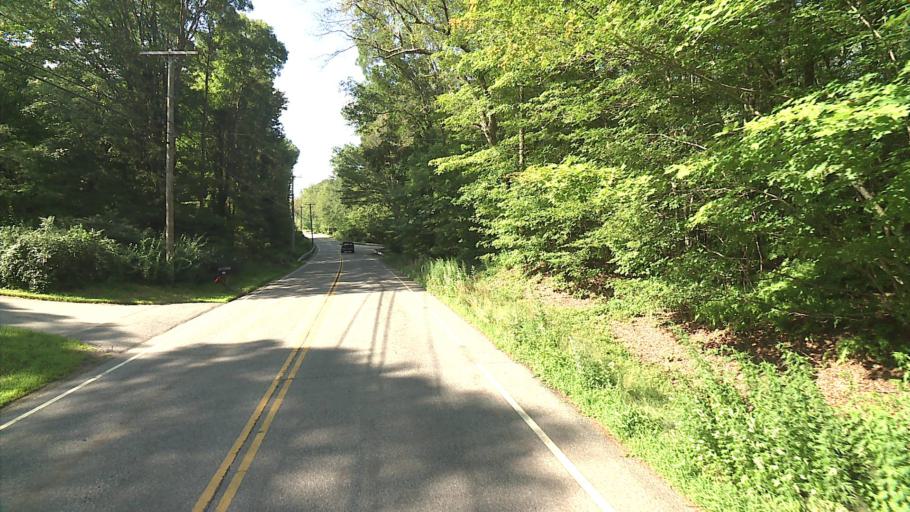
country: US
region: Connecticut
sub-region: New London County
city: Montville Center
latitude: 41.5277
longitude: -72.2065
